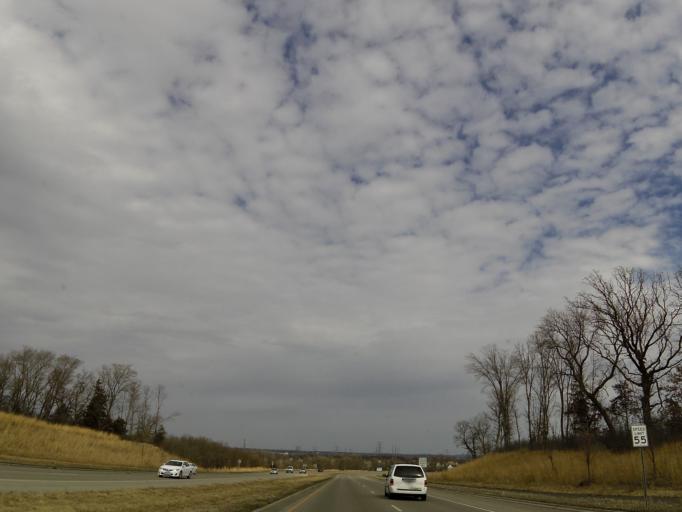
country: US
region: Minnesota
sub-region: Scott County
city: Prior Lake
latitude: 44.7679
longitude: -93.4357
